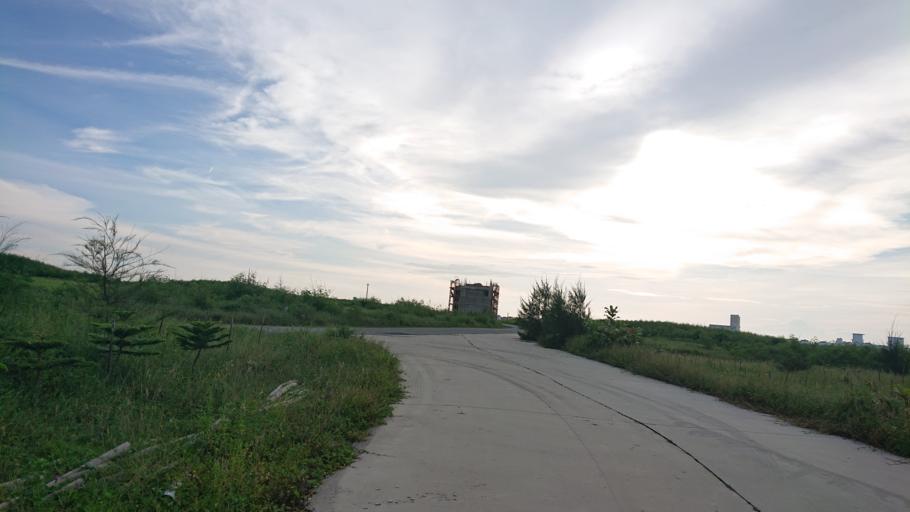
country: TW
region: Taiwan
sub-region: Penghu
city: Ma-kung
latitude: 23.5216
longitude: 119.6080
